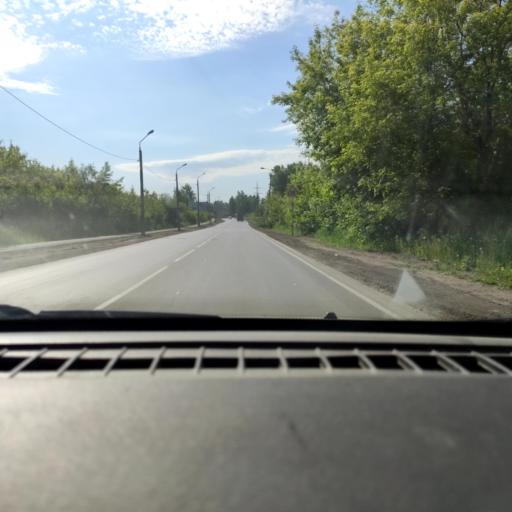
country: RU
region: Perm
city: Krasnokamsk
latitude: 58.0766
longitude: 55.7781
